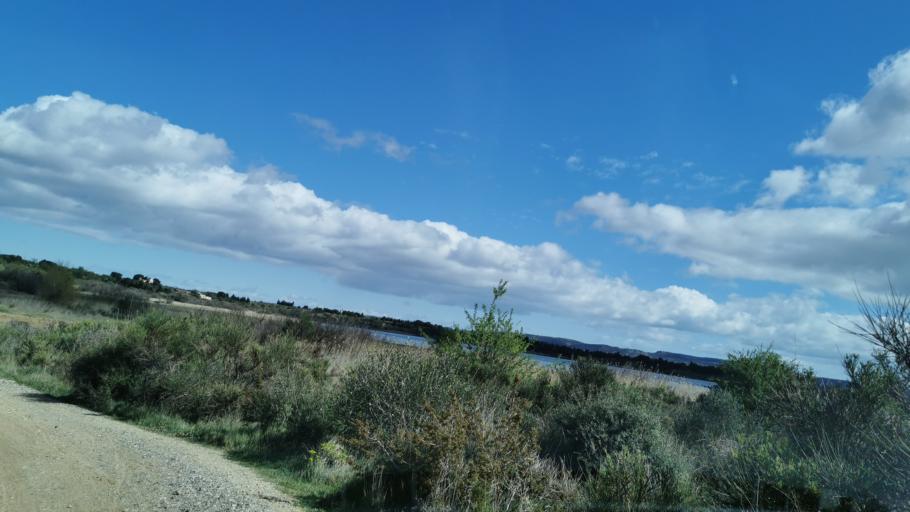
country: FR
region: Languedoc-Roussillon
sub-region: Departement de l'Aude
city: Narbonne
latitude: 43.1473
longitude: 2.9856
